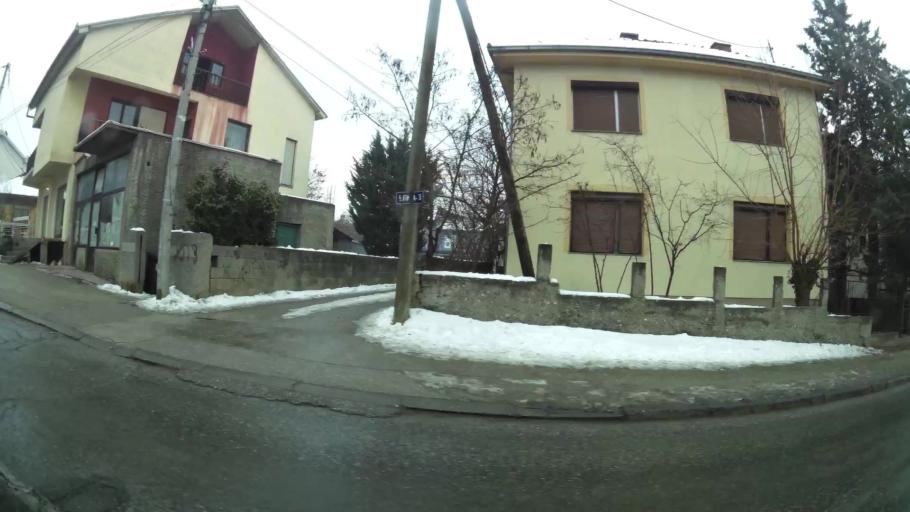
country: MK
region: Saraj
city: Saraj
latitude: 42.0279
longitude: 21.3533
